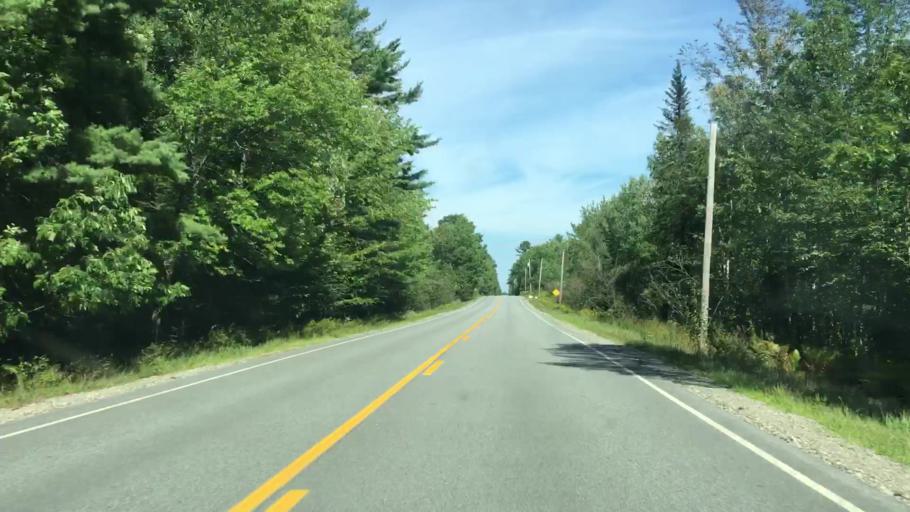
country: US
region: Maine
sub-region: Penobscot County
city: Howland
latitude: 45.2147
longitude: -68.7949
